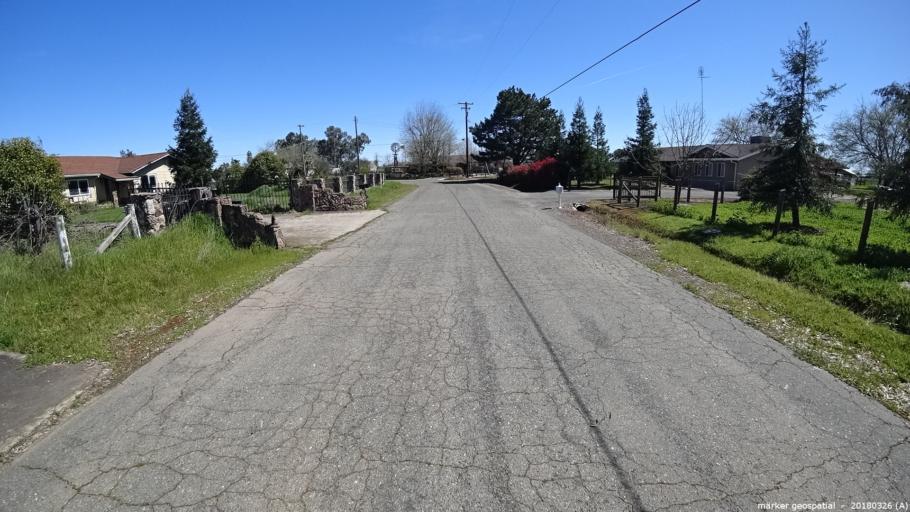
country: US
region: California
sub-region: Sacramento County
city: Wilton
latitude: 38.4570
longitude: -121.2907
